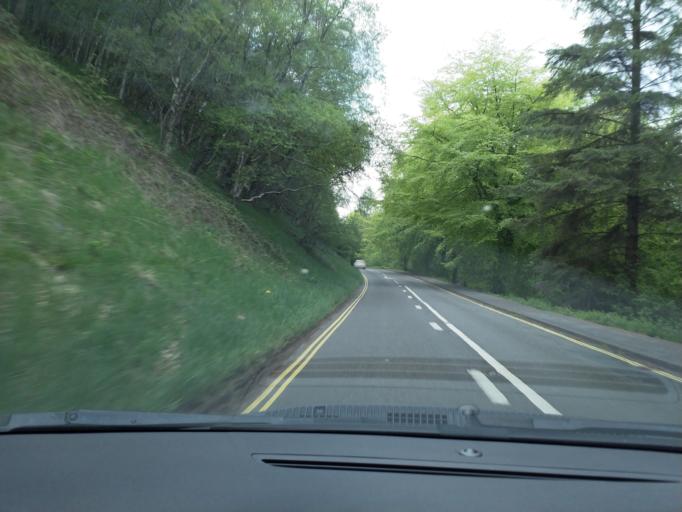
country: GB
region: England
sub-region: Derbyshire
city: Hope Valley
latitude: 53.3870
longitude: -1.7208
